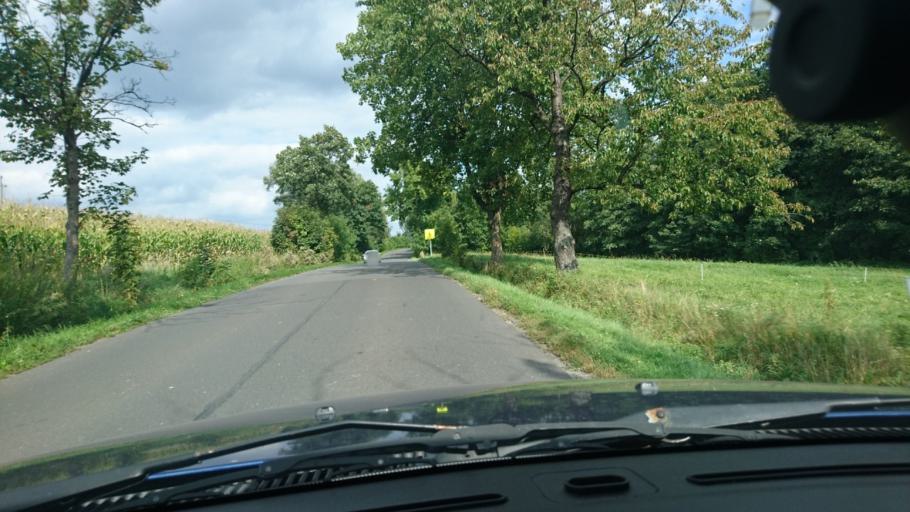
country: PL
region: Silesian Voivodeship
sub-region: Powiat bielski
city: Mazancowice
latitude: 49.8600
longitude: 18.9871
